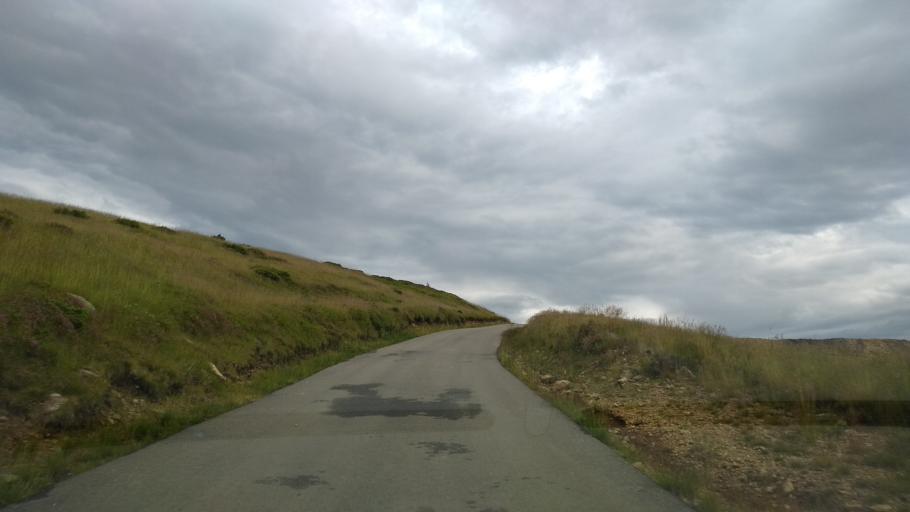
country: RO
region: Hunedoara
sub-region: Municipiul  Vulcan
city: Jiu-Paroseni
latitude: 45.3052
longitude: 23.3121
